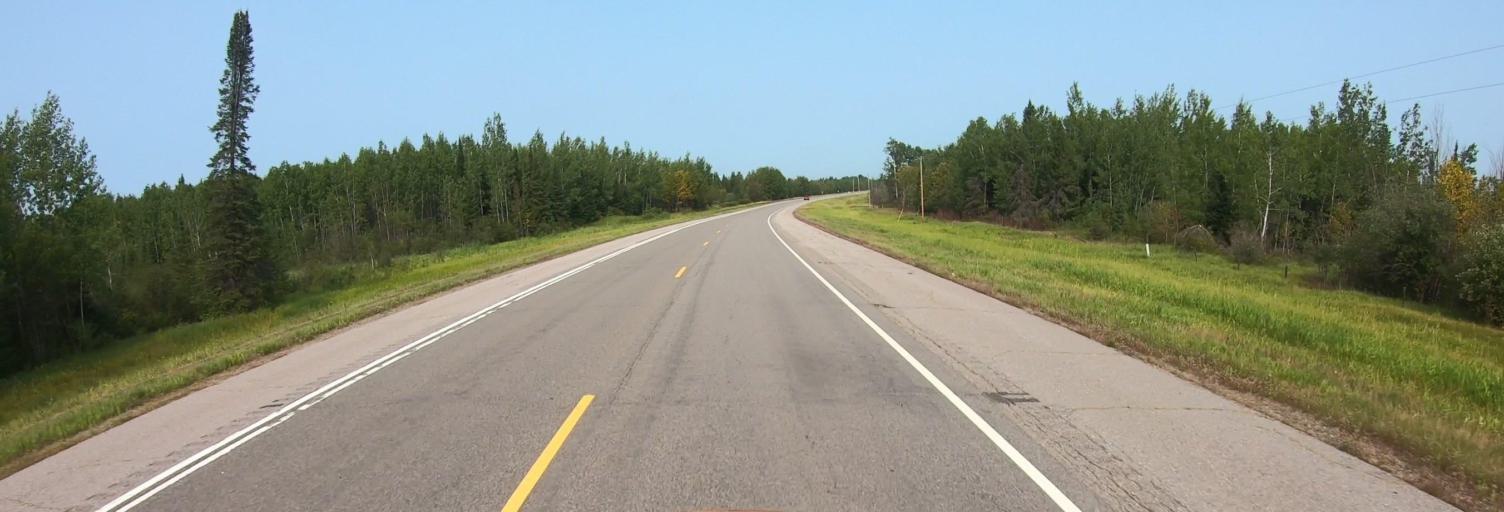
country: US
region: Minnesota
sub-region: Saint Louis County
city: Mountain Iron
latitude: 47.8753
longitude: -92.7569
